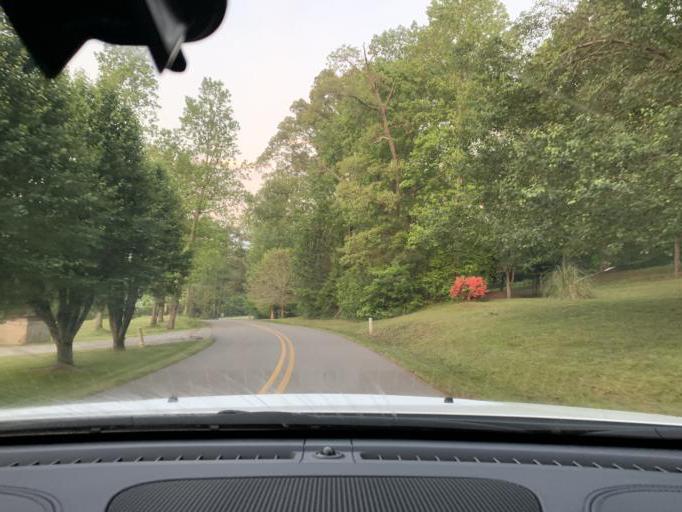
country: US
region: Georgia
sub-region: Dawson County
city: Dawsonville
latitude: 34.3297
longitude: -84.1742
